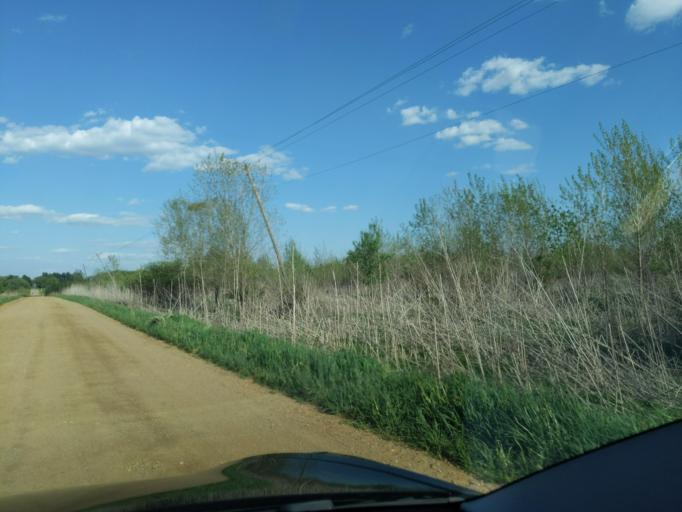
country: US
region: Michigan
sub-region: Eaton County
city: Potterville
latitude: 42.6828
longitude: -84.7277
